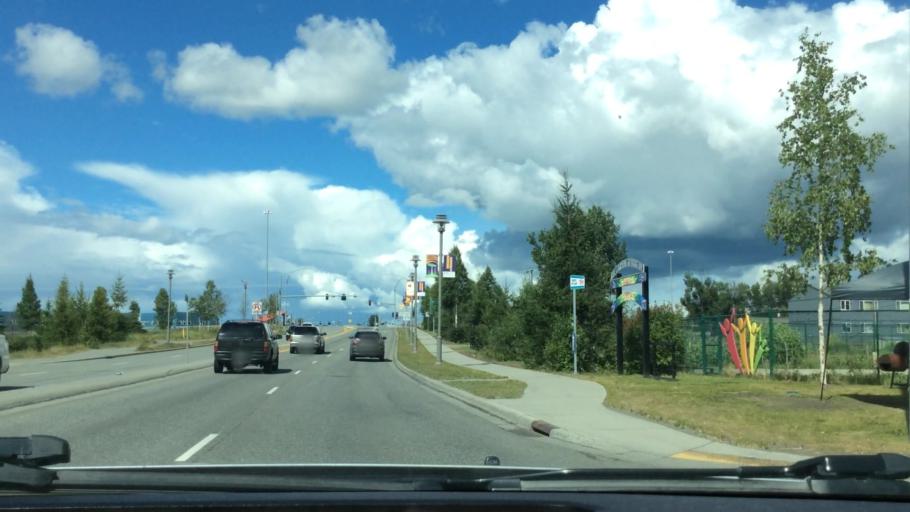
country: US
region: Alaska
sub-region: Anchorage Municipality
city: Anchorage
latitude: 61.2187
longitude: -149.8083
